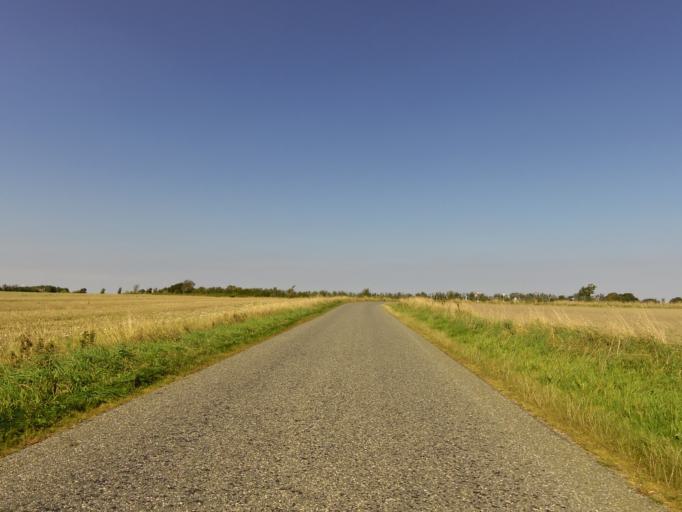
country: DK
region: South Denmark
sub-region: Haderslev Kommune
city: Gram
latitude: 55.3167
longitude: 9.1056
